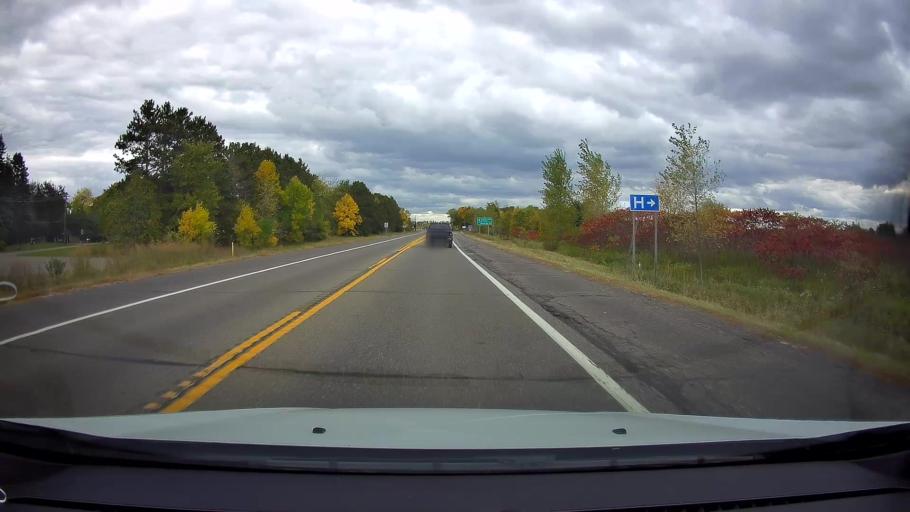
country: US
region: Minnesota
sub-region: Chisago County
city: Chisago City
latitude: 45.3593
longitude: -92.9085
